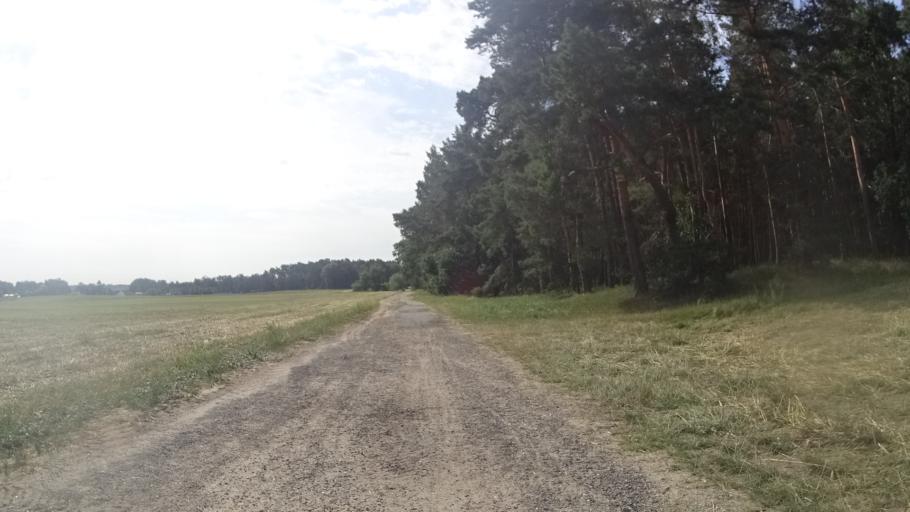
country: DE
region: Brandenburg
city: Brandenburg an der Havel
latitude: 52.3721
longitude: 12.6234
